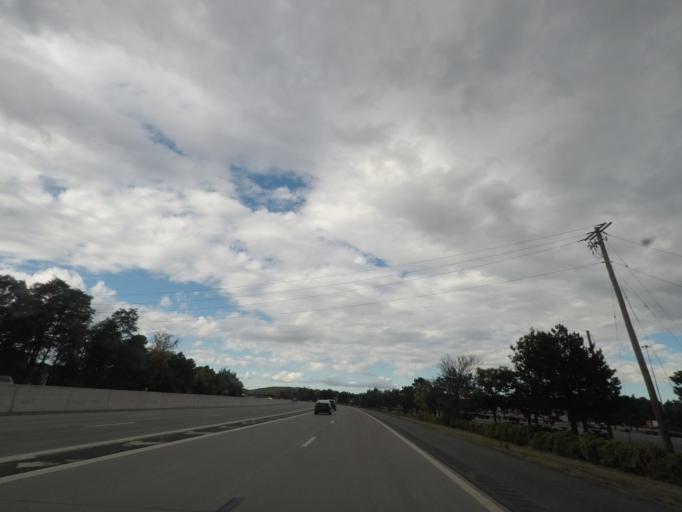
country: US
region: New York
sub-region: Albany County
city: McKownville
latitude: 42.6959
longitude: -73.8443
